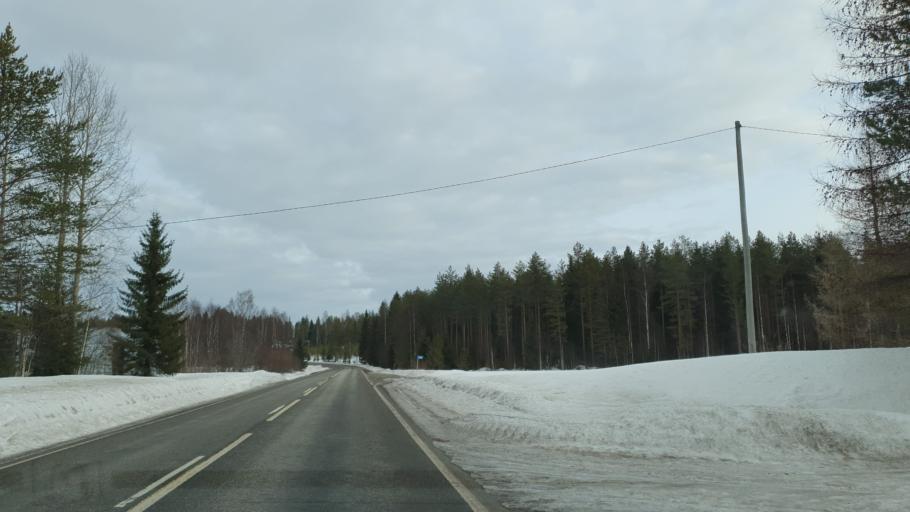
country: FI
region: Kainuu
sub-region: Kajaani
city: Vuokatti
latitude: 64.2415
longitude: 28.0561
